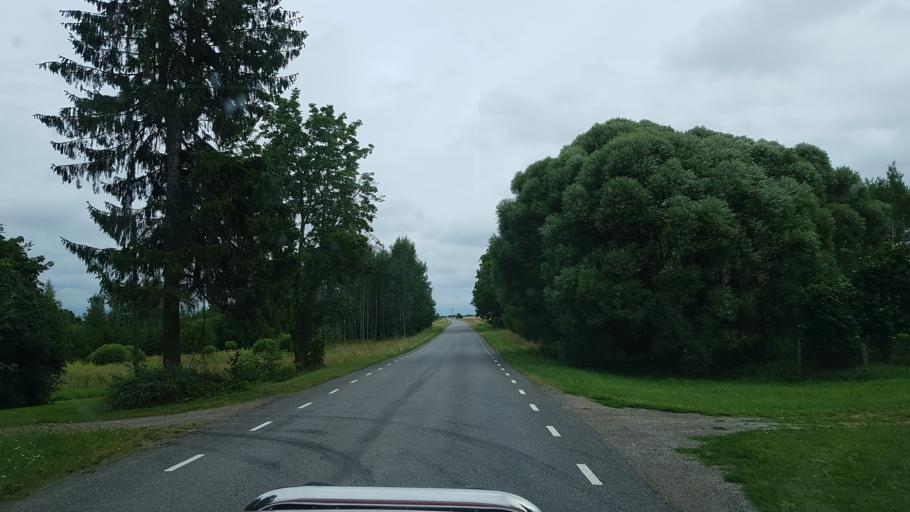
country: EE
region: Ida-Virumaa
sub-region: Kivioli linn
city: Kivioli
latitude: 59.4097
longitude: 27.0043
